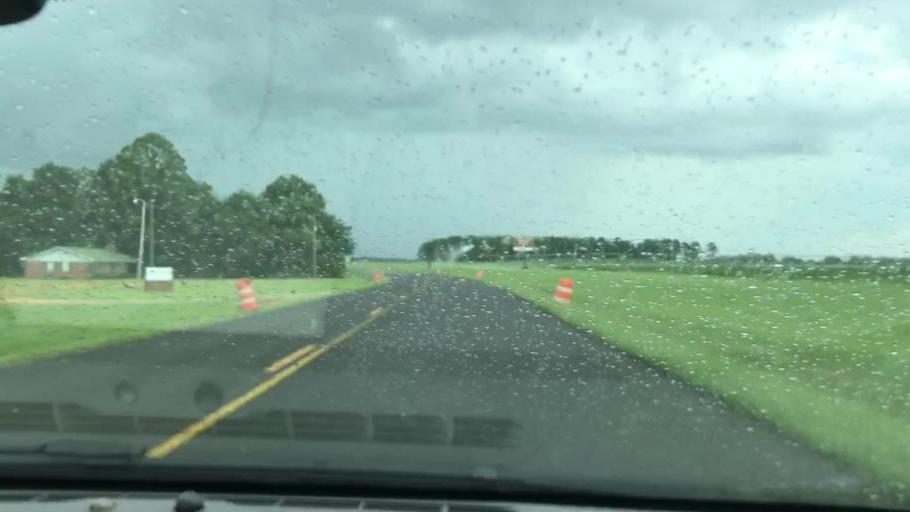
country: US
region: Georgia
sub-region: Clay County
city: Fort Gaines
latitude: 31.4873
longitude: -85.0173
